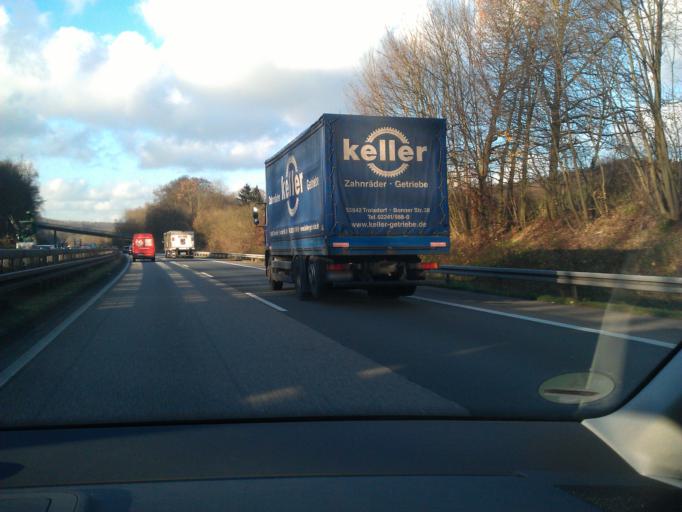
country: DE
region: North Rhine-Westphalia
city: Sprockhovel
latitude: 51.3690
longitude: 7.2738
